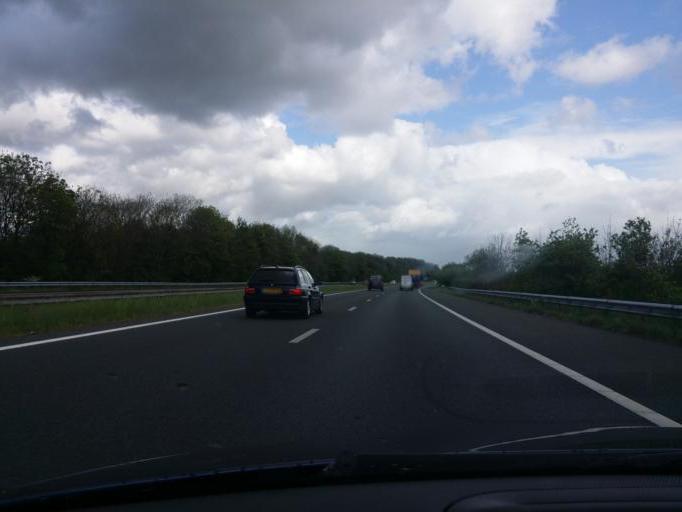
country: NL
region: Groningen
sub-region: Gemeente Hoogezand-Sappemeer
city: Hoogezand
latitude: 53.1989
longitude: 6.6908
